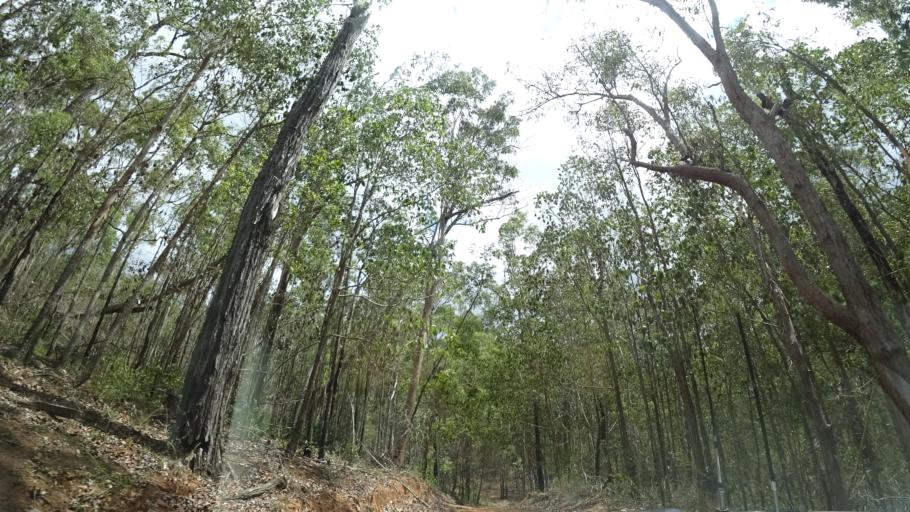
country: AU
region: Queensland
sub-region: Moreton Bay
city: Highvale
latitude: -27.4337
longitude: 152.7520
